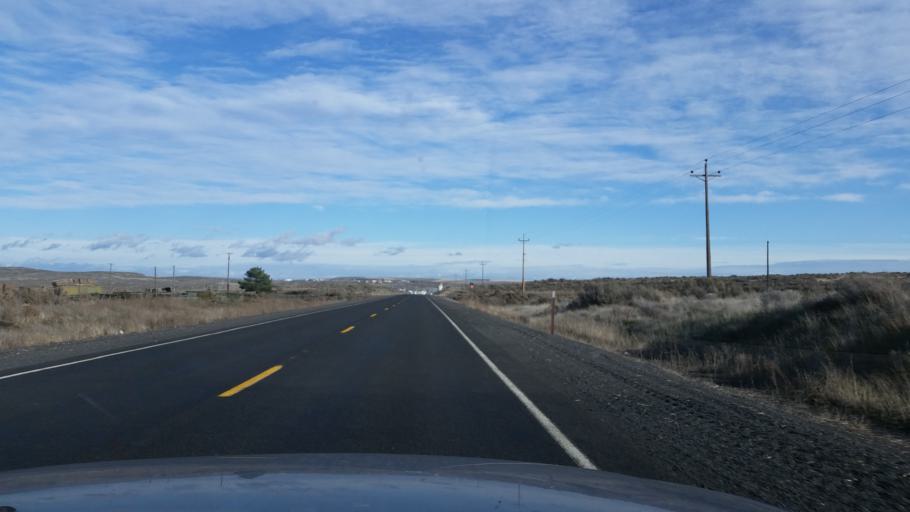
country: US
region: Washington
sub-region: Adams County
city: Ritzville
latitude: 47.3236
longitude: -118.7252
